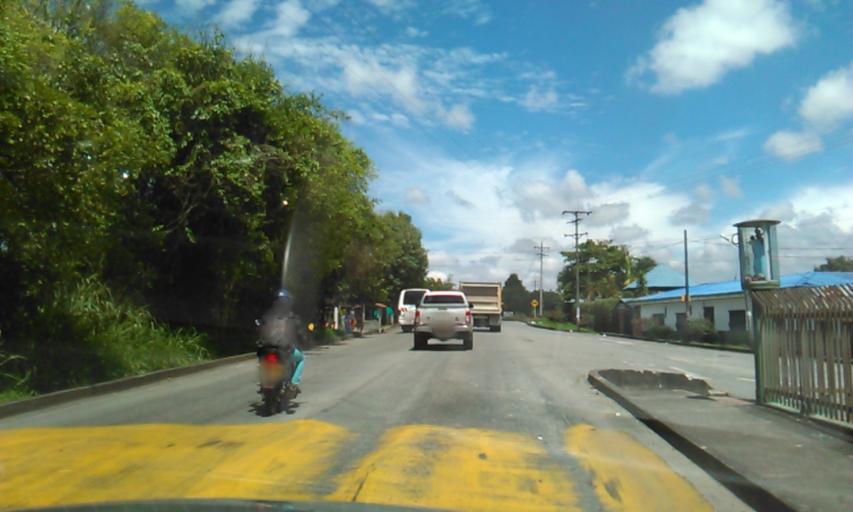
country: CO
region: Quindio
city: Cordoba
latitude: 4.4323
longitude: -75.7176
